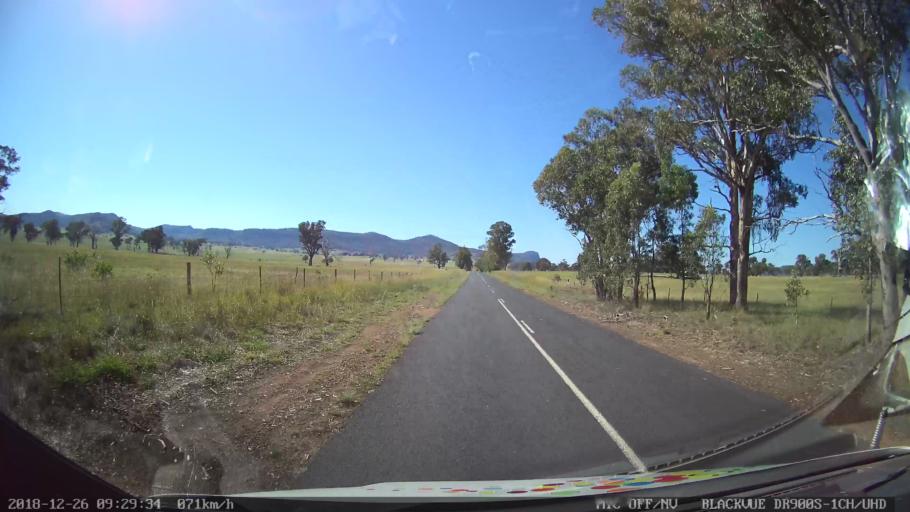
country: AU
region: New South Wales
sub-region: Mid-Western Regional
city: Kandos
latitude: -32.8543
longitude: 150.0280
